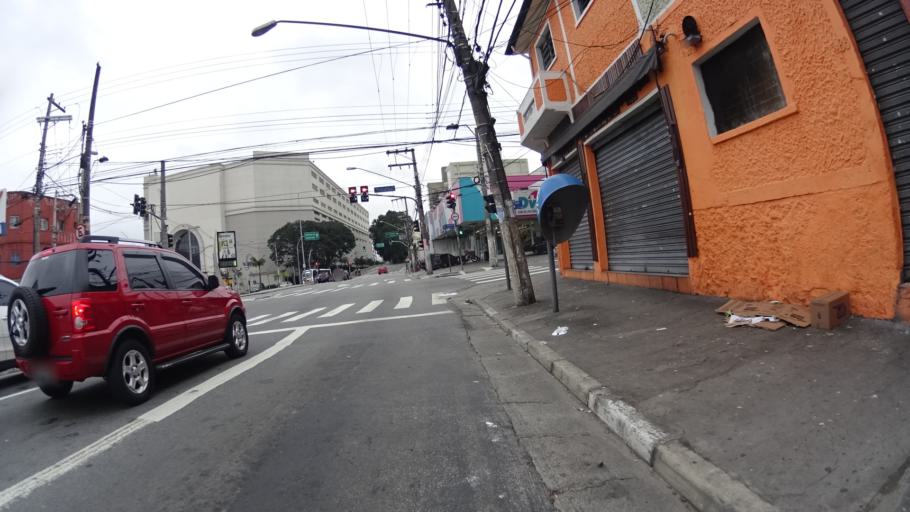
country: BR
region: Sao Paulo
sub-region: Guarulhos
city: Guarulhos
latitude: -23.4818
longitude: -46.6033
